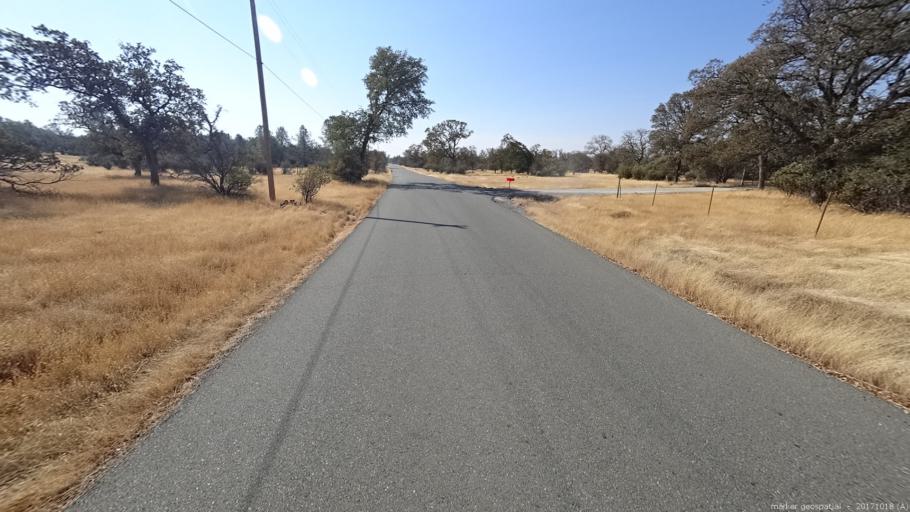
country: US
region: California
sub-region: Shasta County
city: Palo Cedro
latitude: 40.5403
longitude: -122.1135
